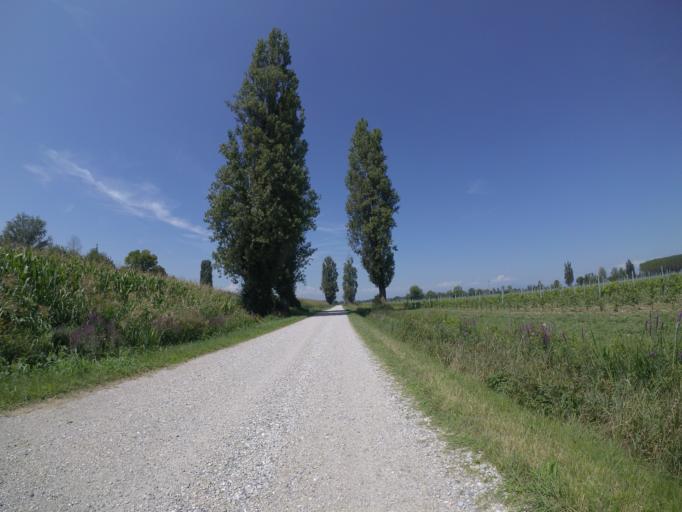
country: IT
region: Friuli Venezia Giulia
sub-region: Provincia di Udine
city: Varmo
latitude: 45.9234
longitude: 13.0010
